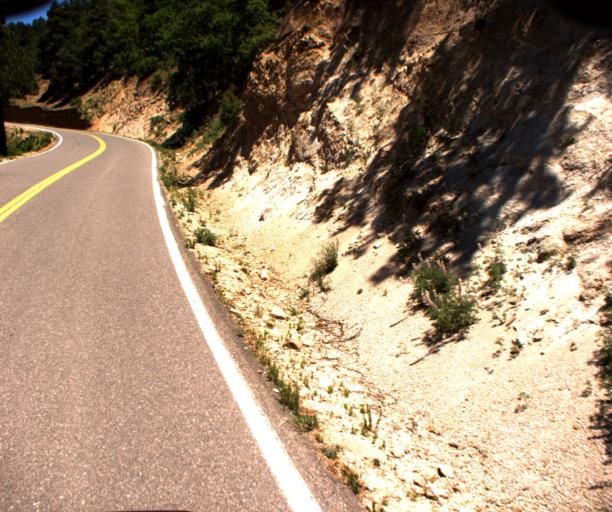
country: US
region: Arizona
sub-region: Graham County
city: Swift Trail Junction
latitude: 32.6252
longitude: -109.8340
